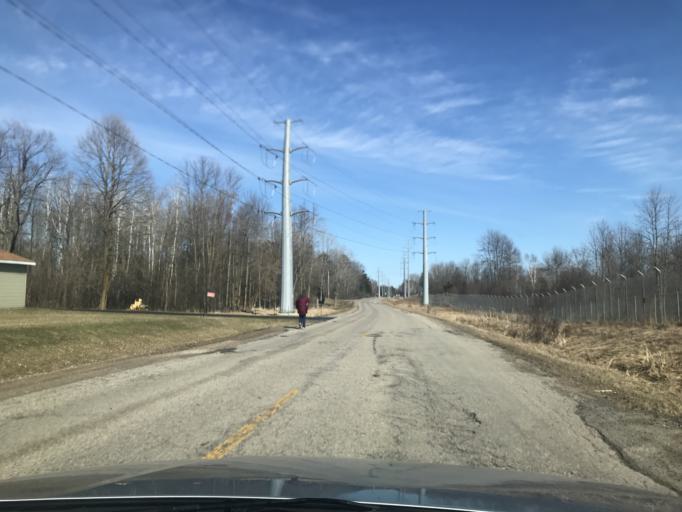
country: US
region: Michigan
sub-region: Menominee County
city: Menominee
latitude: 45.1445
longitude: -87.6288
